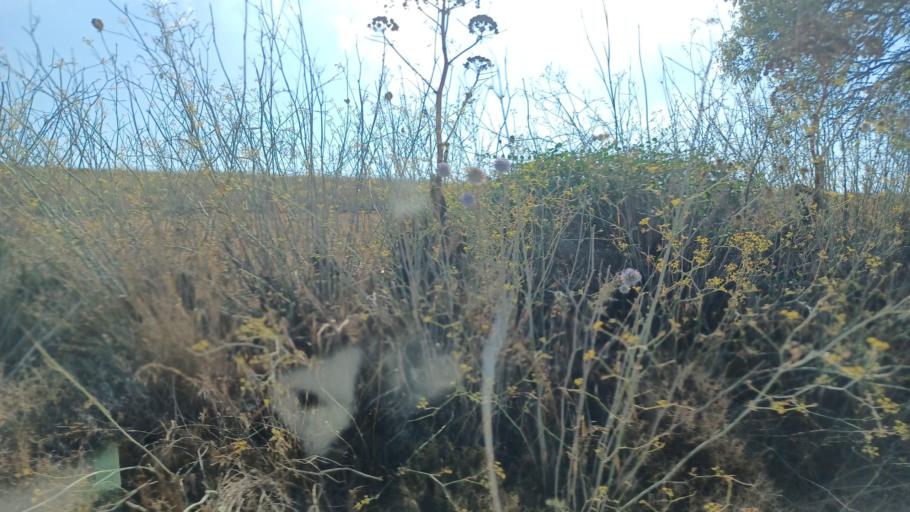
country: CY
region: Pafos
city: Pegeia
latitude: 34.9023
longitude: 32.4227
